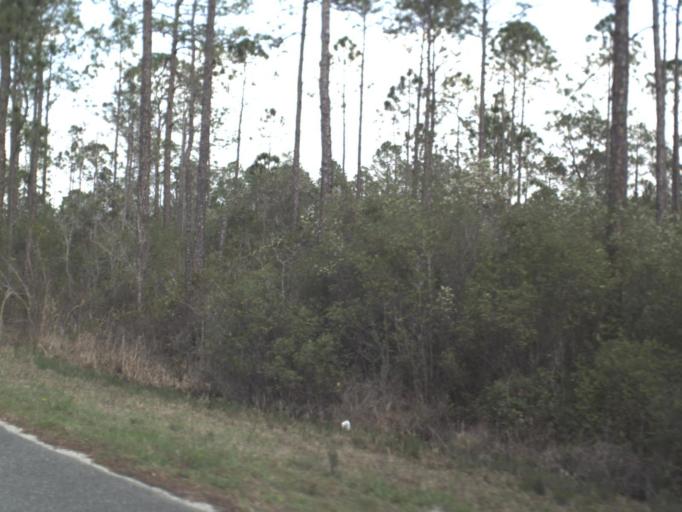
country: US
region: Florida
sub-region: Franklin County
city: Apalachicola
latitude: 29.9736
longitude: -84.9750
